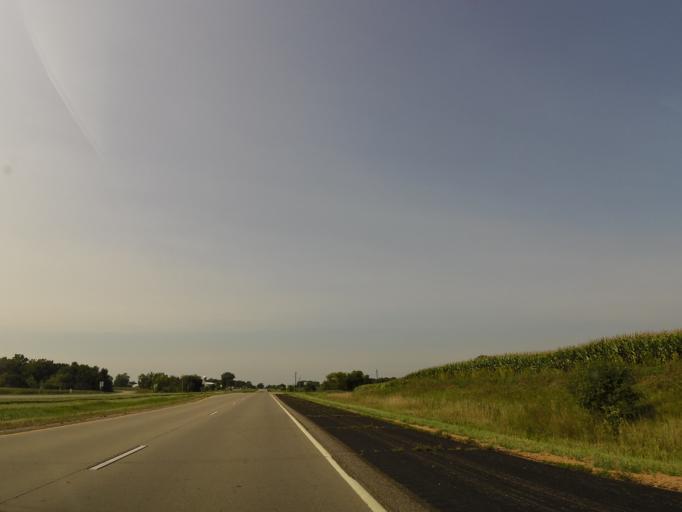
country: US
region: Minnesota
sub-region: Carver County
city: Cologne
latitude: 44.7718
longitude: -93.7652
